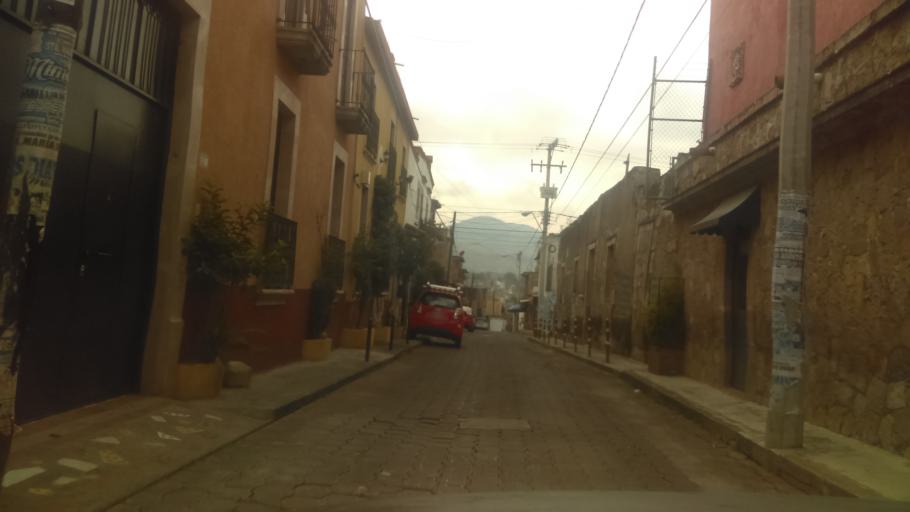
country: MX
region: Michoacan
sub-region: Morelia
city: Montana Monarca (Punta Altozano)
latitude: 19.6725
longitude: -101.1917
